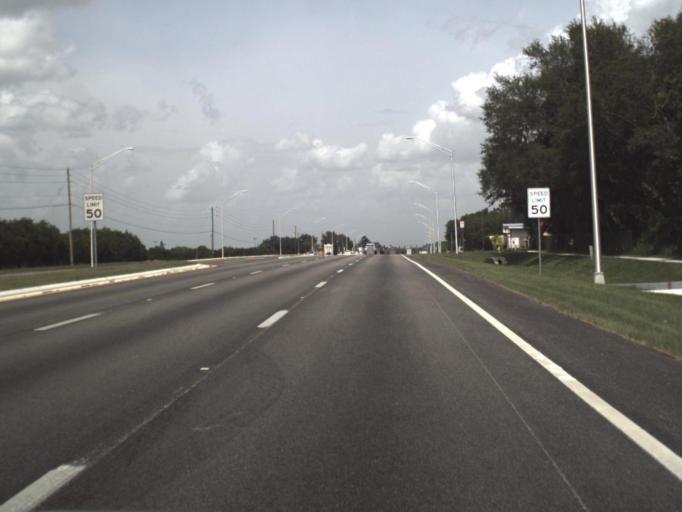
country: US
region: Florida
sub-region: Highlands County
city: Avon Park
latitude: 27.6120
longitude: -81.5144
